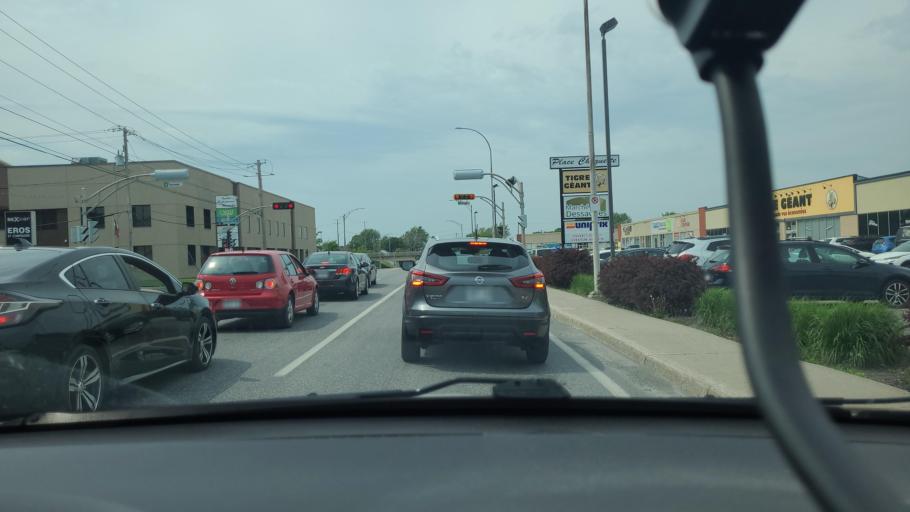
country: CA
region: Quebec
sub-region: Monteregie
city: Saint-Hyacinthe
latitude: 45.6233
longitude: -72.9597
